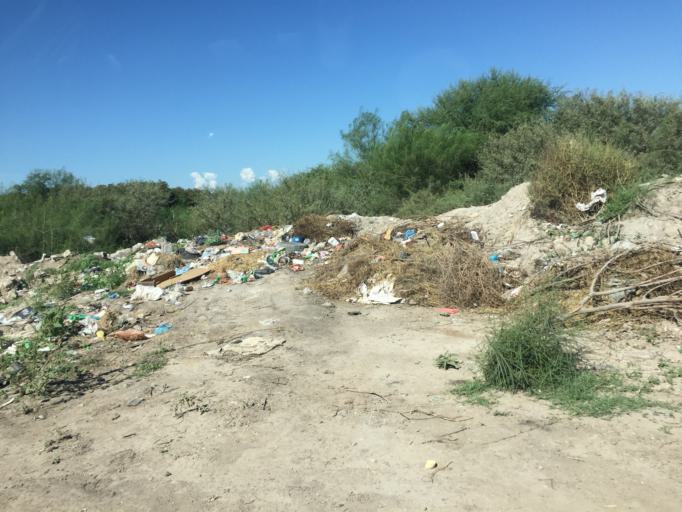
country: MX
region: Durango
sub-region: Gomez Palacio
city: San Felipe
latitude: 25.7255
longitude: -103.3712
